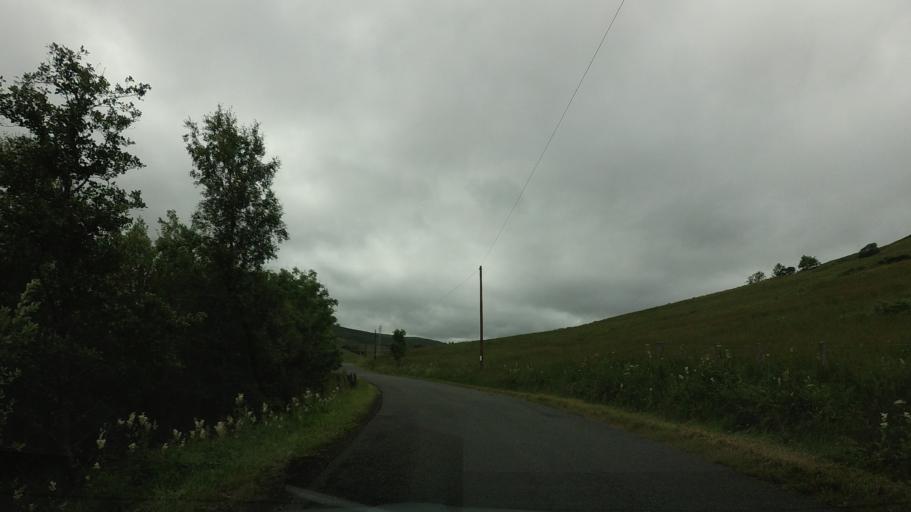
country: GB
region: Scotland
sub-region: The Scottish Borders
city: Innerleithen
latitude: 55.4457
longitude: -3.1047
